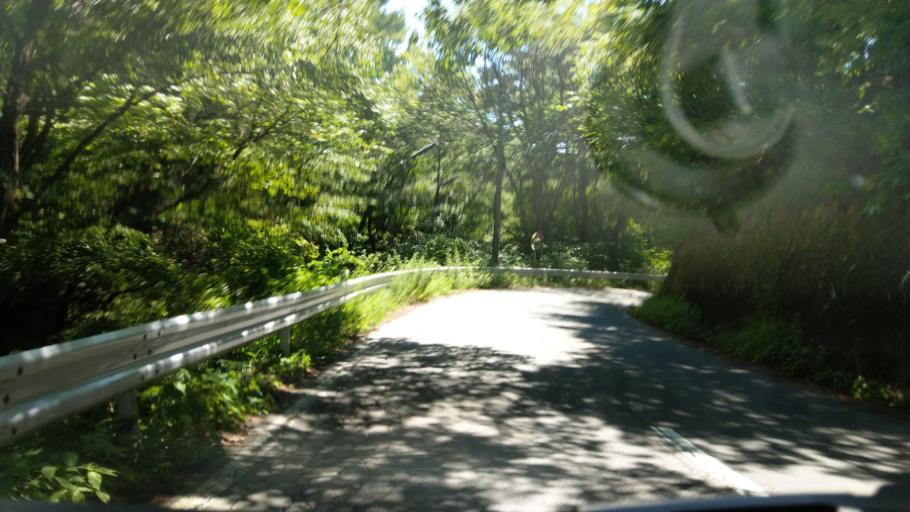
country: JP
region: Nagano
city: Komoro
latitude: 36.3714
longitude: 138.4612
